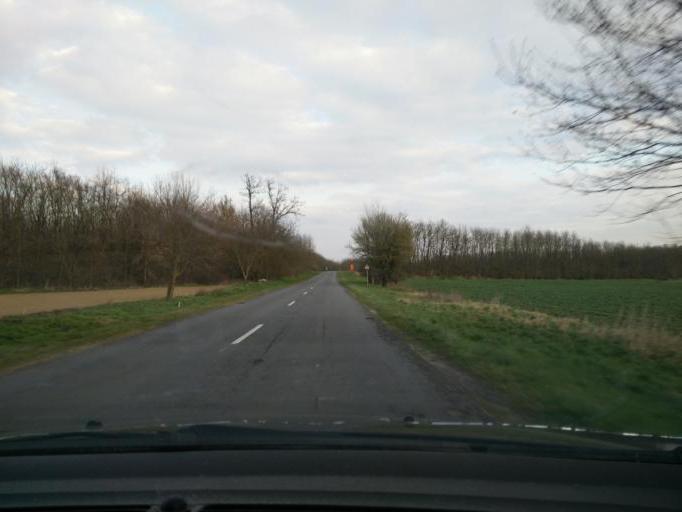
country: HU
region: Zala
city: Turje
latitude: 46.9923
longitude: 17.0650
